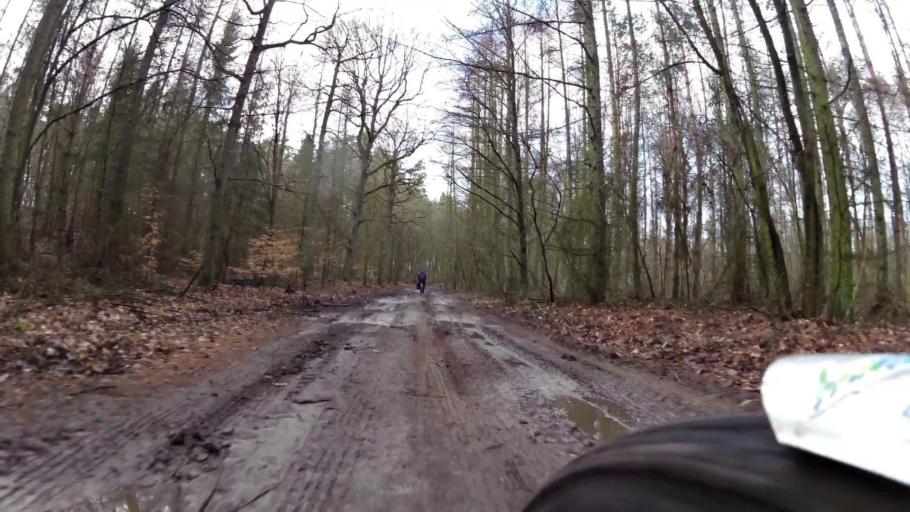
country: PL
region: West Pomeranian Voivodeship
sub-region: Powiat kamienski
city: Wolin
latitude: 53.8653
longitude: 14.7117
